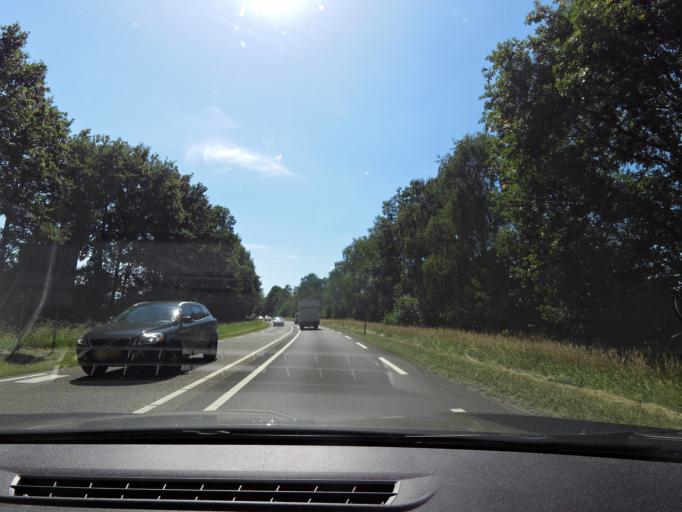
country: NL
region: Gelderland
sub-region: Oost Gelre
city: Lichtenvoorde
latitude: 52.0320
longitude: 6.6177
